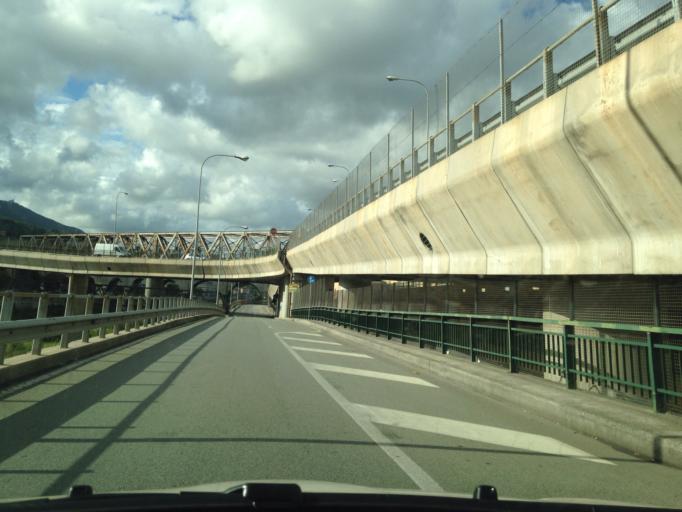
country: IT
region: Liguria
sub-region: Provincia di Genova
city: Genoa
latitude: 44.4368
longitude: 8.8903
